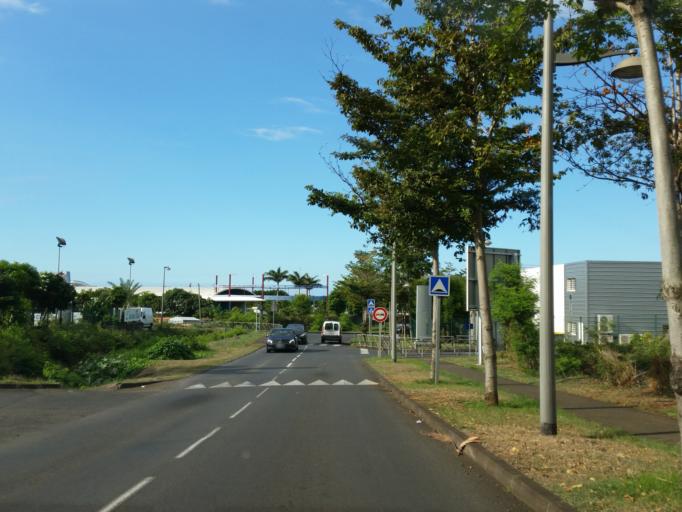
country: RE
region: Reunion
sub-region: Reunion
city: Sainte-Marie
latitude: -20.9044
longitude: 55.4983
